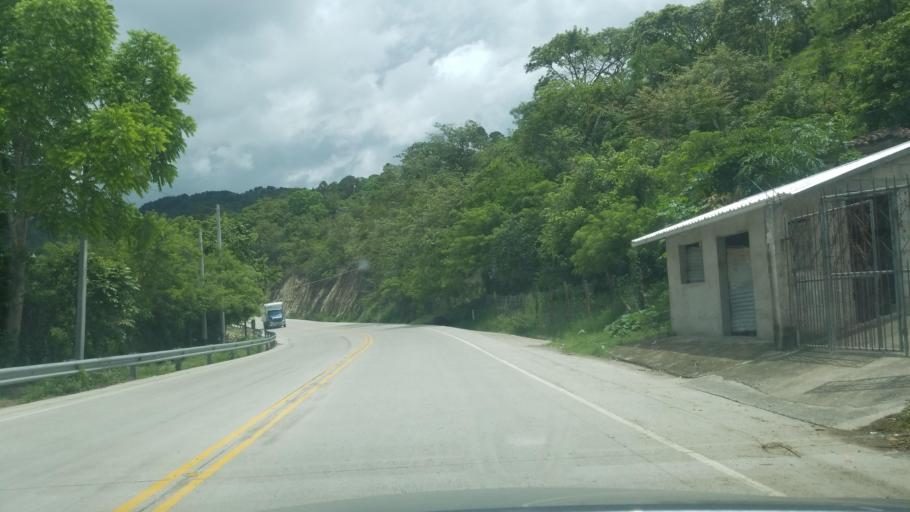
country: HN
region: Copan
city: San Jeronimo
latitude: 14.9888
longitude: -88.8467
